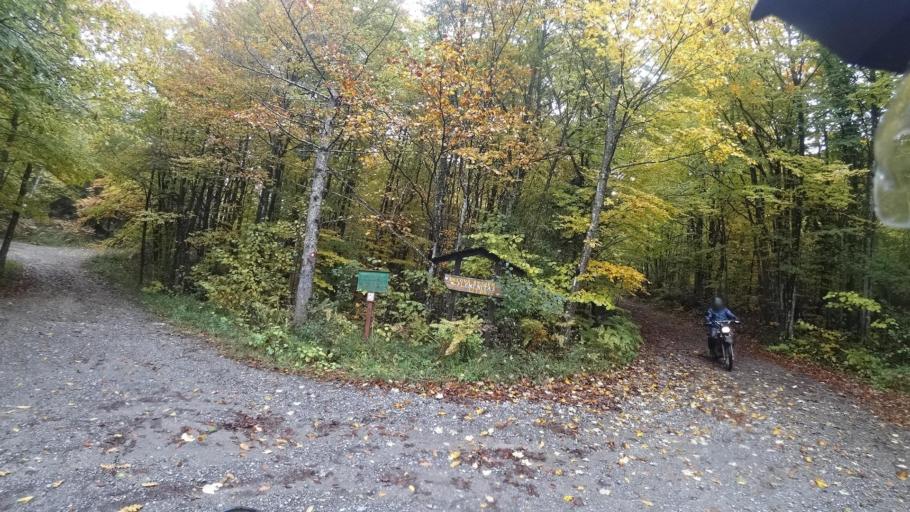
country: HR
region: Primorsko-Goranska
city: Vrbovsko
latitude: 45.4755
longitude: 15.0427
